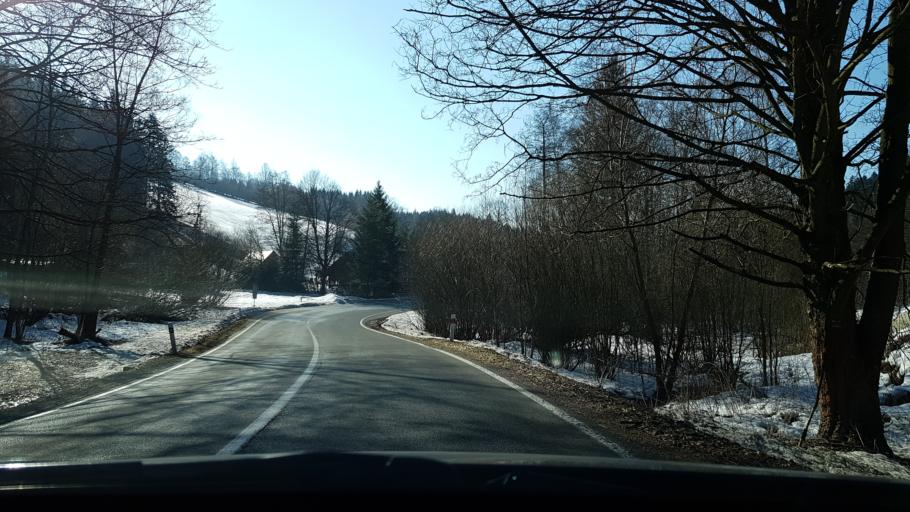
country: CZ
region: Olomoucky
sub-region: Okres Sumperk
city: Stare Mesto
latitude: 50.1352
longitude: 17.0128
